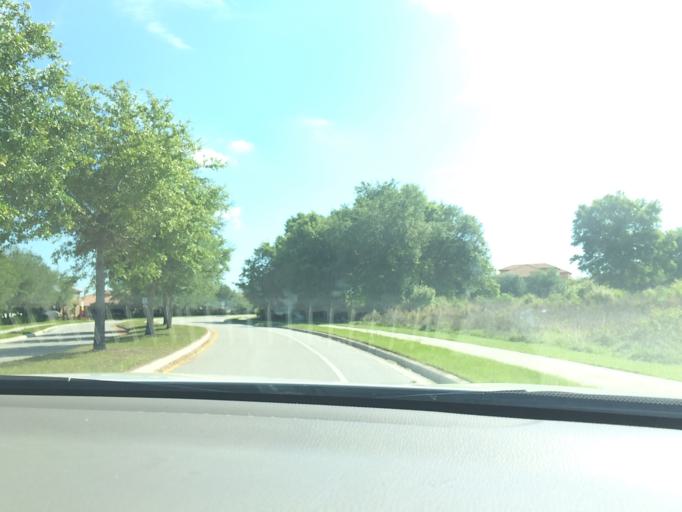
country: US
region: Florida
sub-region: Sarasota County
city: North Sarasota
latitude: 27.3923
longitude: -82.5187
